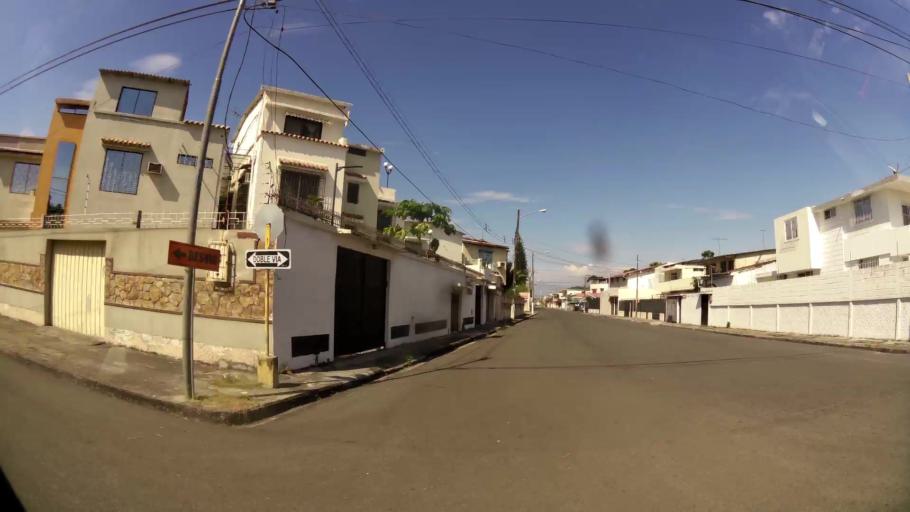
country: EC
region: Guayas
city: Guayaquil
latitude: -2.2224
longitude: -79.8932
